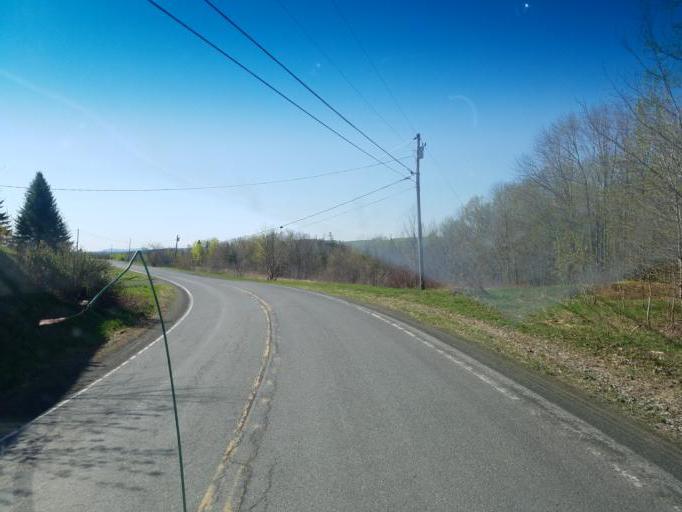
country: US
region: Maine
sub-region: Aroostook County
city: Caribou
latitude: 46.8577
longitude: -68.2084
